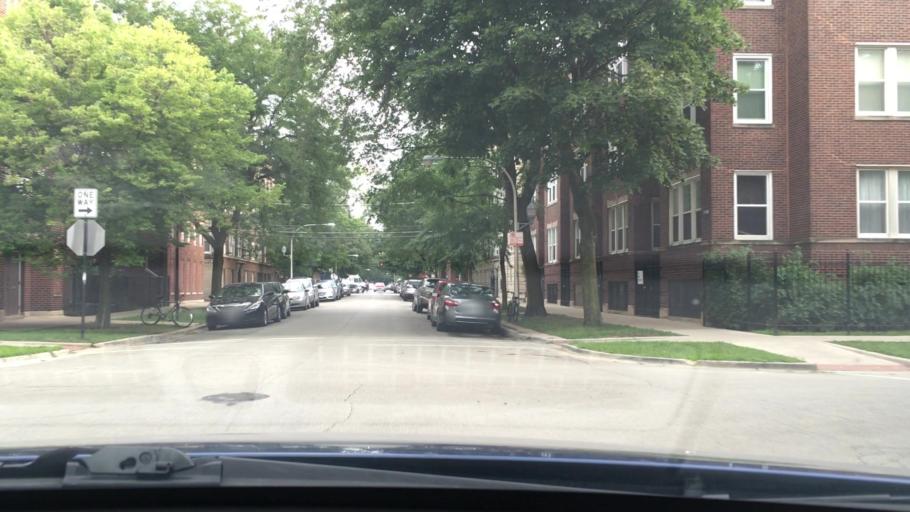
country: US
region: Illinois
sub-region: Cook County
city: Evanston
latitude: 41.9637
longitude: -87.6524
